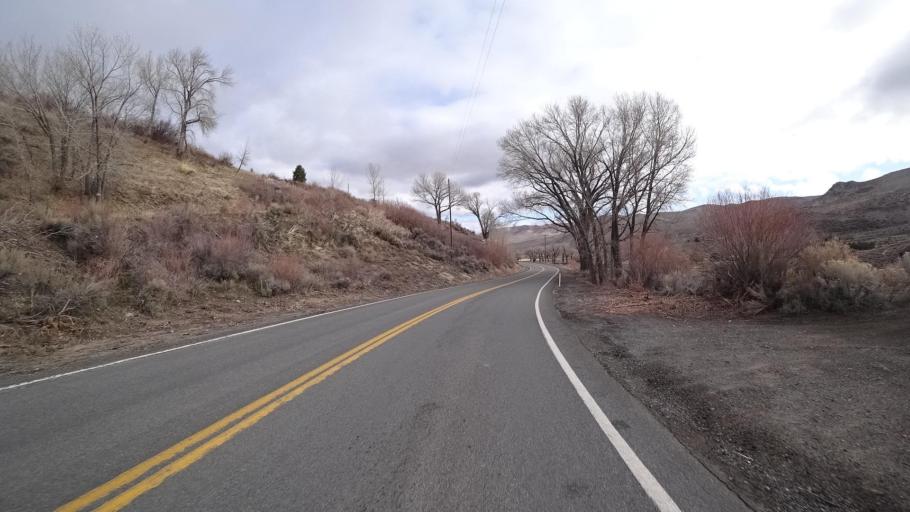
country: US
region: Nevada
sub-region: Washoe County
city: Cold Springs
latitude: 39.8346
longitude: -119.9371
